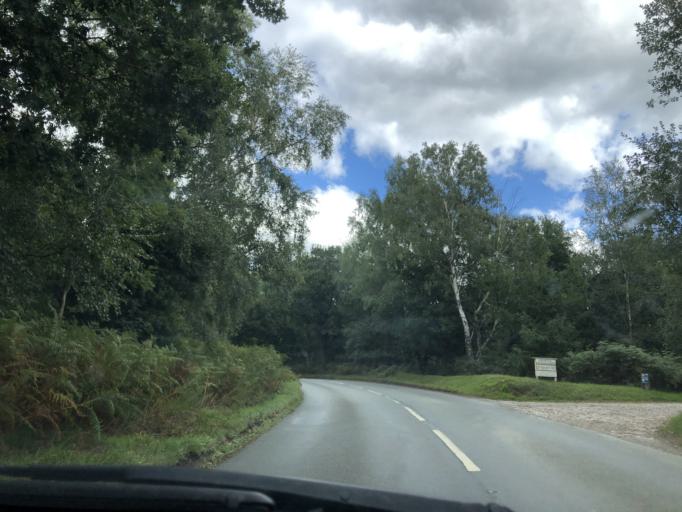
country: GB
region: England
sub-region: East Sussex
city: Forest Row
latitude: 51.0400
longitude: 0.0667
